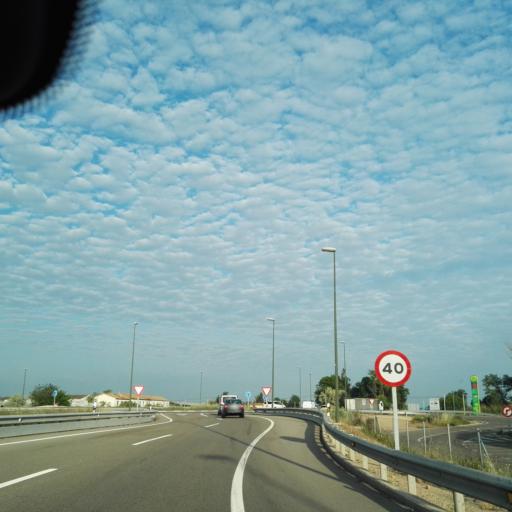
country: ES
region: Aragon
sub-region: Provincia de Zaragoza
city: Oliver-Valdefierro, Oliver, Valdefierro
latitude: 41.6610
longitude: -0.9525
